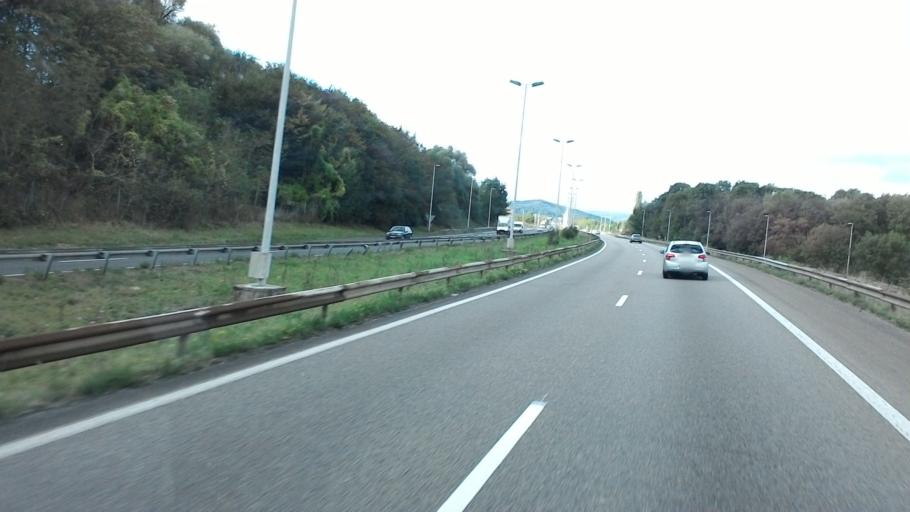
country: FR
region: Lorraine
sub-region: Departement de Meurthe-et-Moselle
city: Belleville
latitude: 48.8134
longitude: 6.1131
